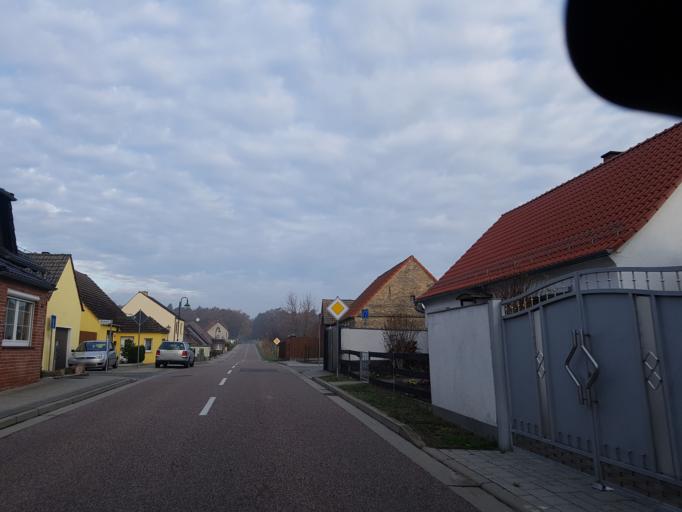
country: DE
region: Saxony-Anhalt
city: Kropstadt
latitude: 51.9378
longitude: 12.7571
